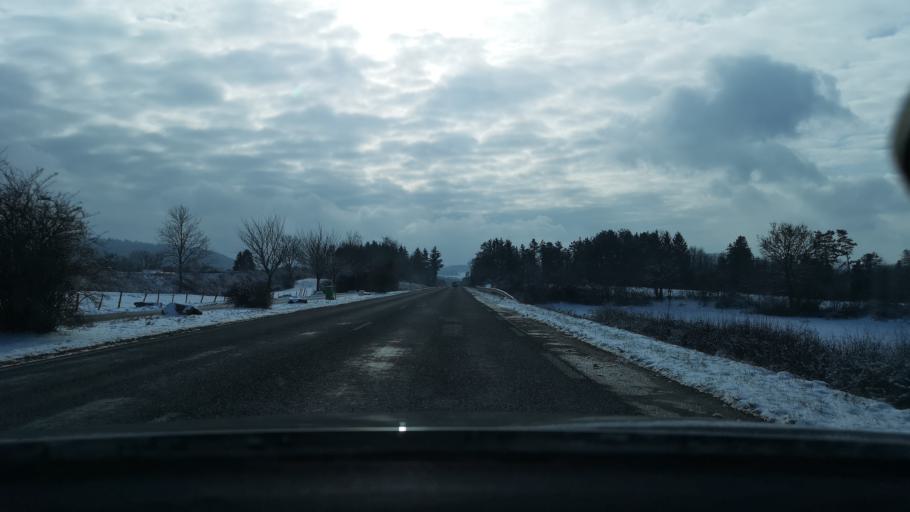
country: FR
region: Franche-Comte
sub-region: Departement du Jura
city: Orgelet
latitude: 46.5537
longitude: 5.5965
